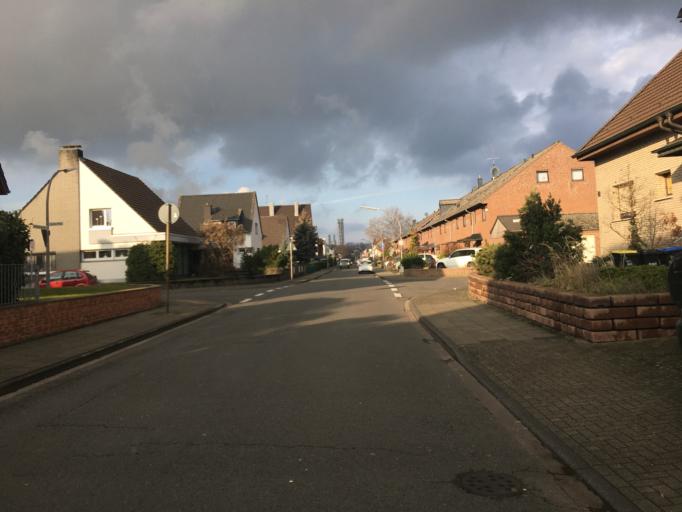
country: DE
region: North Rhine-Westphalia
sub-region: Regierungsbezirk Dusseldorf
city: Dormagen
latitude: 51.0631
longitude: 6.8557
